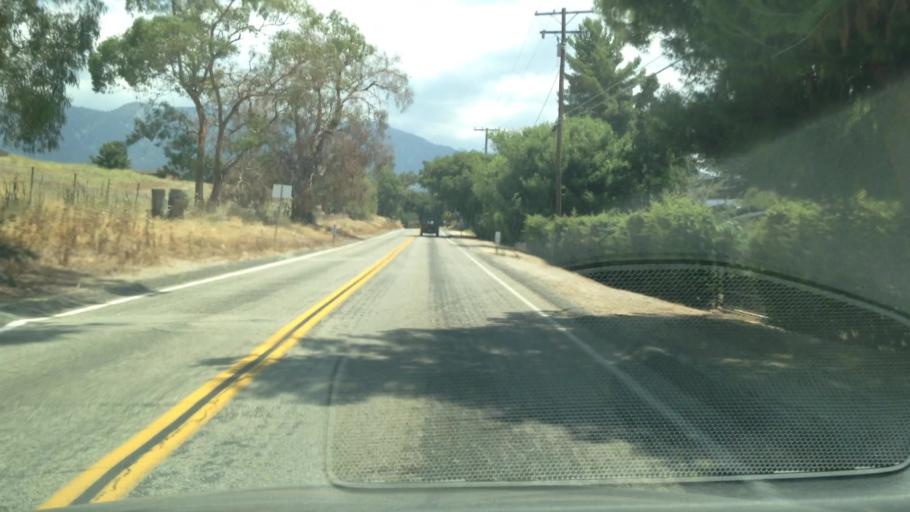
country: US
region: California
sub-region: Riverside County
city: Cherry Valley
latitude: 33.9861
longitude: -116.9687
